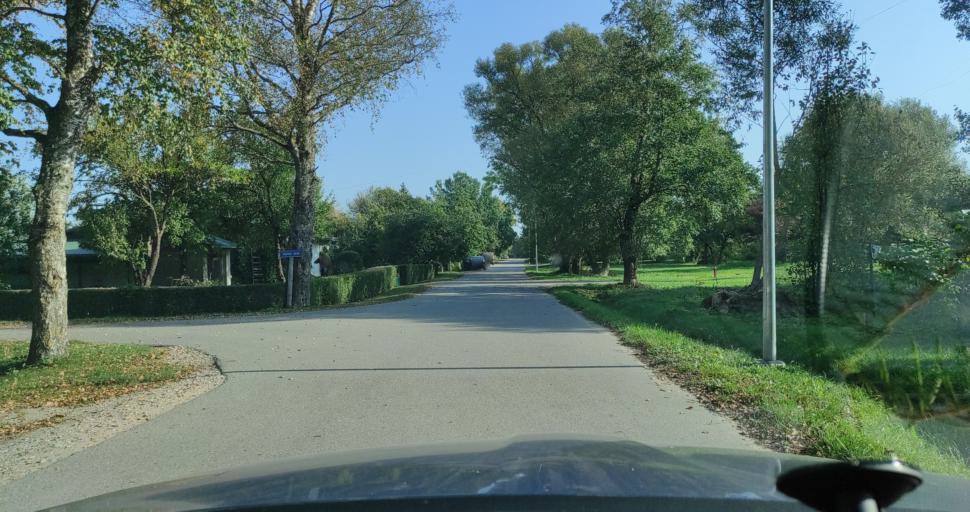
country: LV
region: Ventspils Rajons
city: Piltene
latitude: 57.2286
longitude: 21.6096
